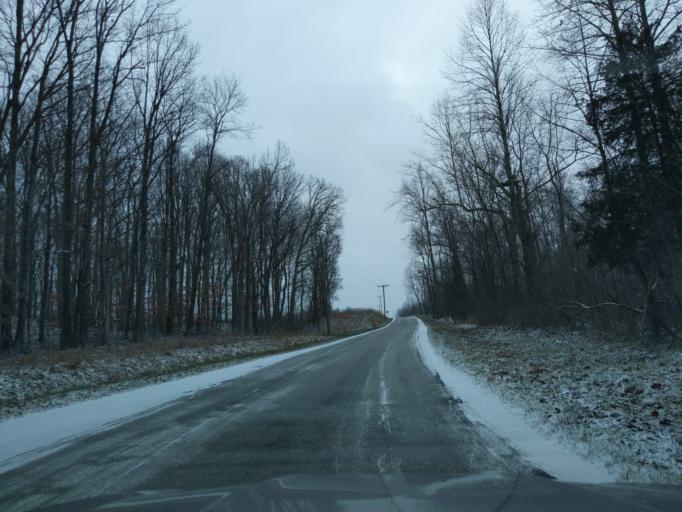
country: US
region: Indiana
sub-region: Decatur County
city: Greensburg
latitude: 39.2455
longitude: -85.4686
